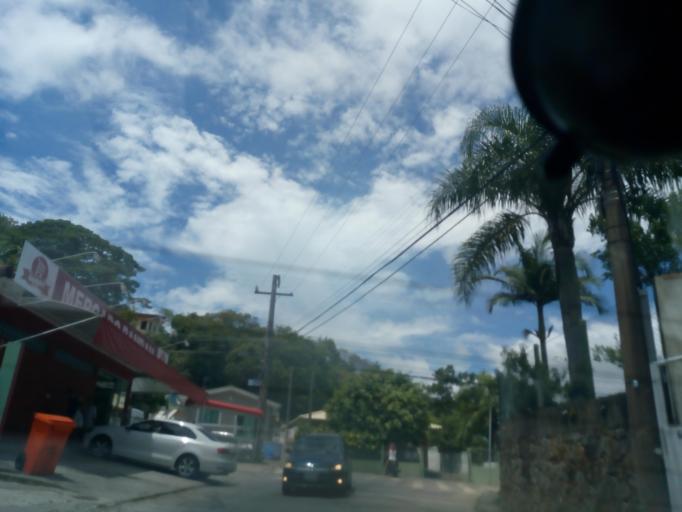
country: BR
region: Santa Catarina
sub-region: Florianopolis
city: Itacorubi
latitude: -27.3968
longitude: -48.4244
